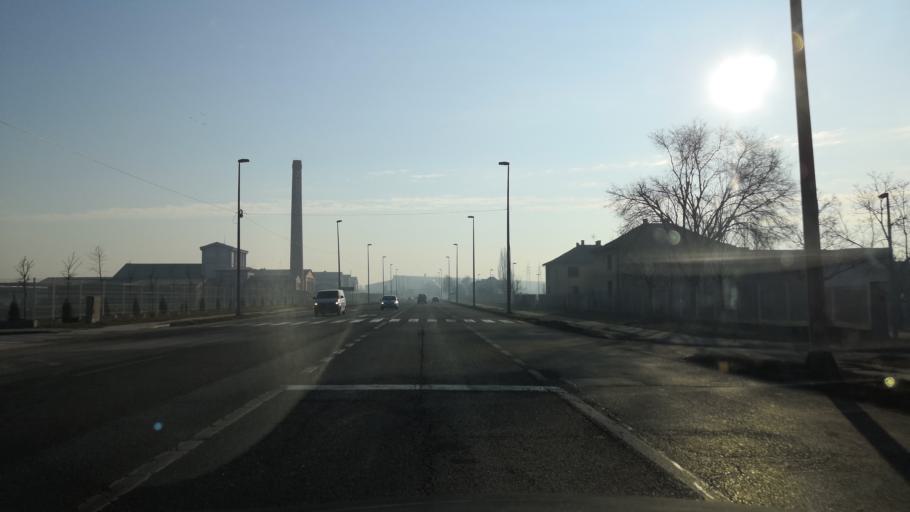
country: RS
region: Central Serbia
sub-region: Macvanski Okrug
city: Sabac
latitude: 44.7480
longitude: 19.7146
